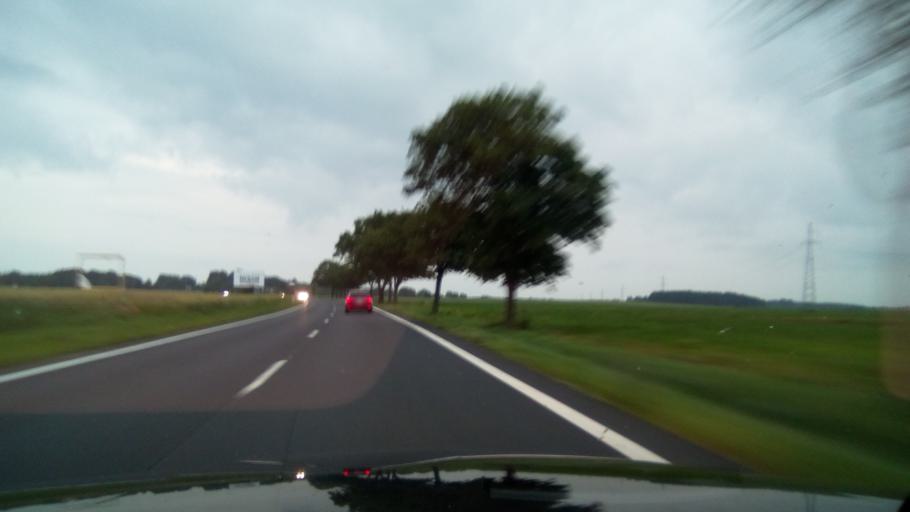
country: PL
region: Greater Poland Voivodeship
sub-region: Powiat poznanski
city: Pobiedziska
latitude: 52.4970
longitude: 17.3380
